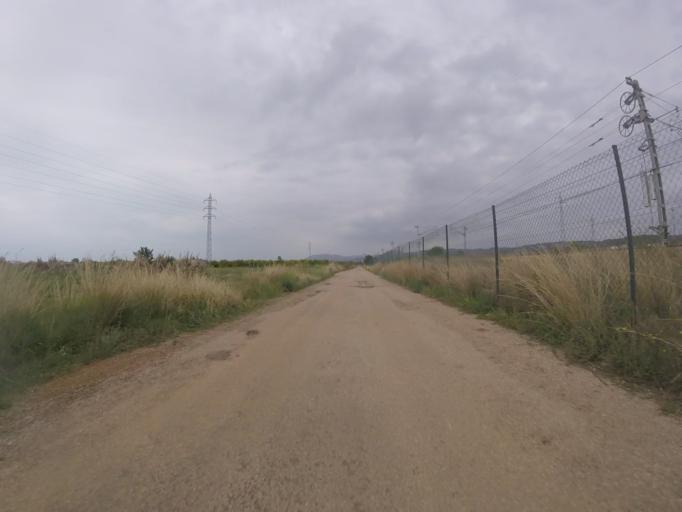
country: ES
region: Valencia
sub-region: Provincia de Castello
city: Torreblanca
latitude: 40.2178
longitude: 0.2054
